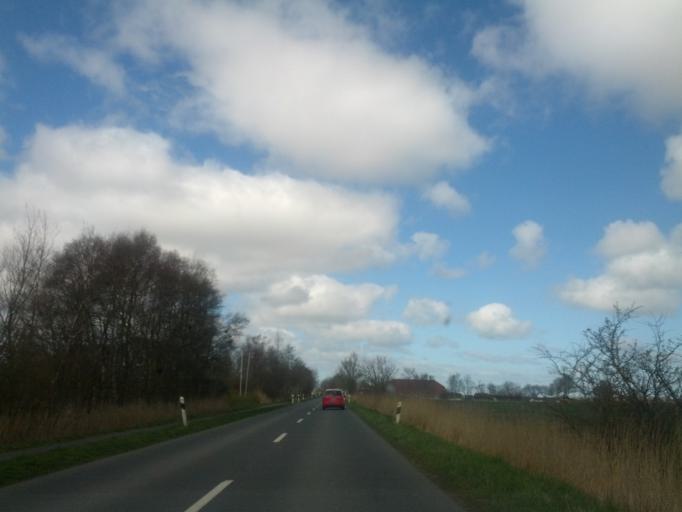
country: DE
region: Lower Saxony
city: Esens
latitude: 53.6594
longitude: 7.6048
